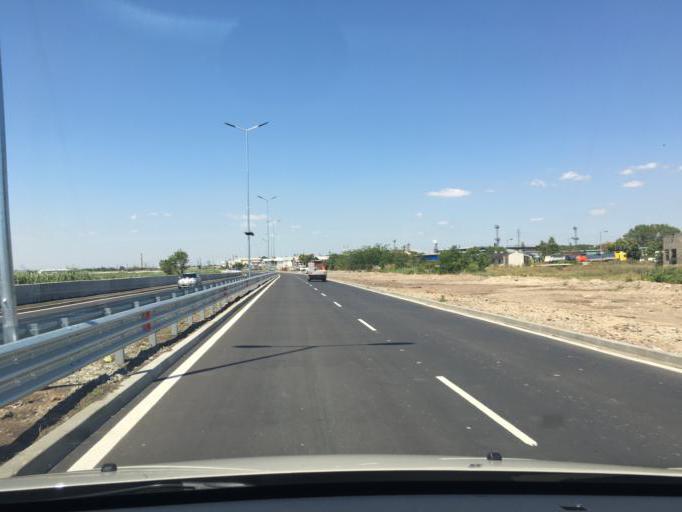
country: BG
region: Burgas
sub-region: Obshtina Burgas
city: Burgas
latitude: 42.5085
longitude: 27.4431
